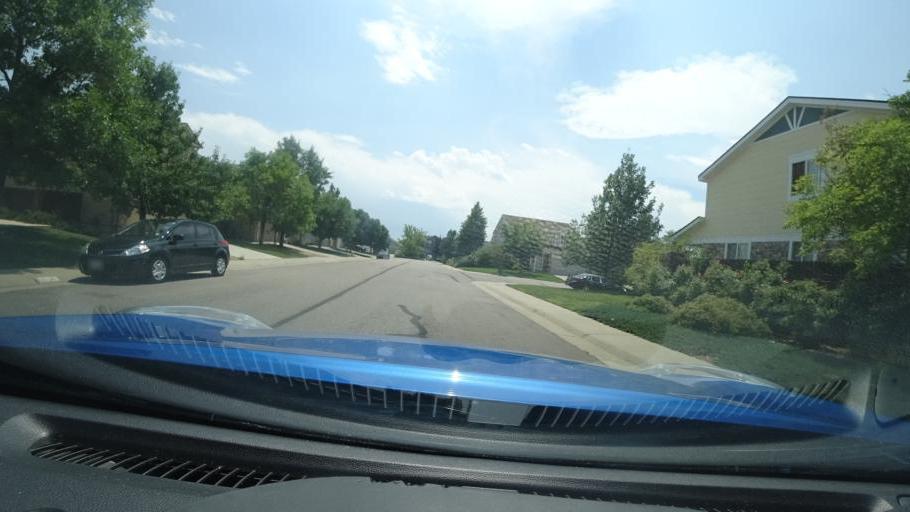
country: US
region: Colorado
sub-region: Adams County
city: Aurora
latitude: 39.6719
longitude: -104.7550
